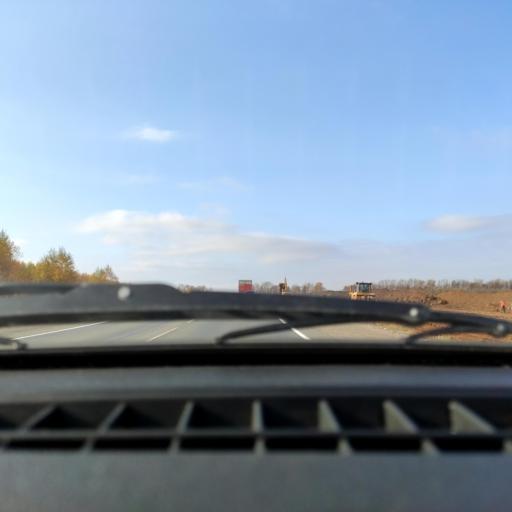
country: RU
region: Bashkortostan
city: Iglino
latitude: 54.7321
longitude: 56.2638
